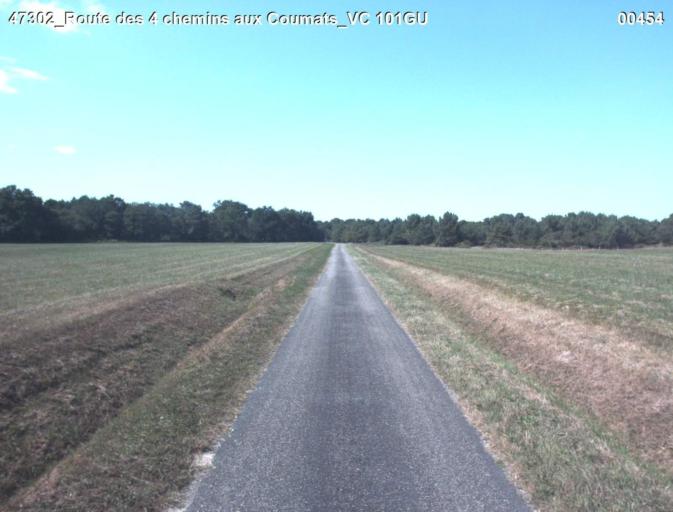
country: FR
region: Aquitaine
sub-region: Departement des Landes
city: Gabarret
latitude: 44.0183
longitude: 0.0869
